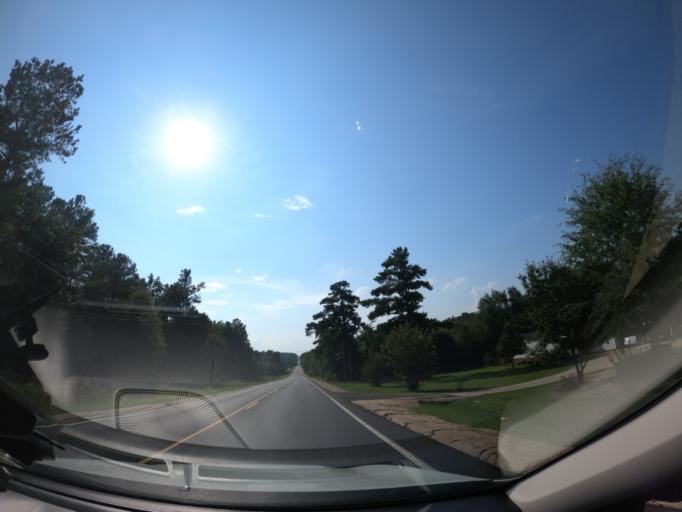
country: US
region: South Carolina
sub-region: Aiken County
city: New Ellenton
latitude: 33.3957
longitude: -81.7437
